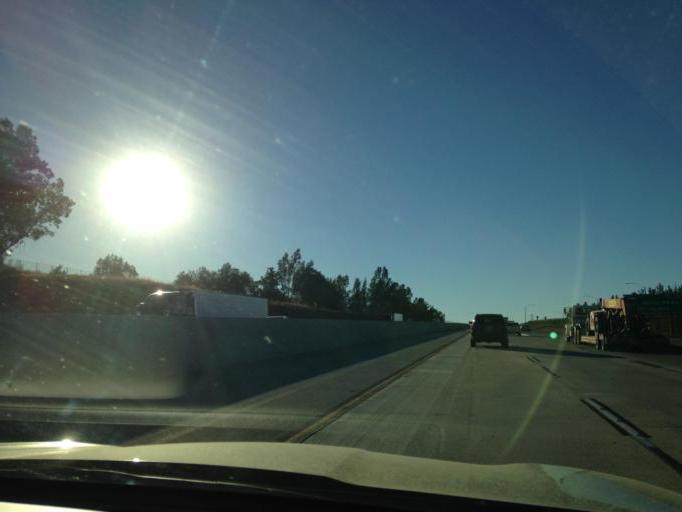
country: US
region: California
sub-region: Riverside County
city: Cherry Valley
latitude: 33.9524
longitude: -117.0122
